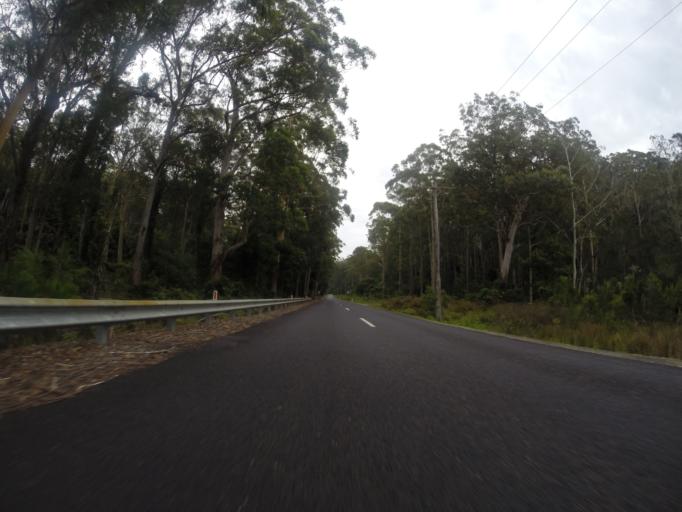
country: AU
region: New South Wales
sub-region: Eurobodalla
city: Batemans Bay
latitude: -35.6572
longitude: 150.2729
